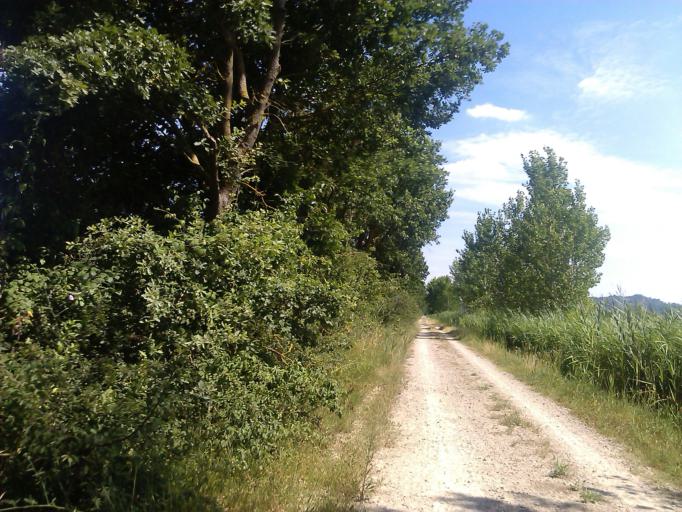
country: IT
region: Tuscany
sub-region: Provincia di Siena
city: Chiusi
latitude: 43.0644
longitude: 11.9312
